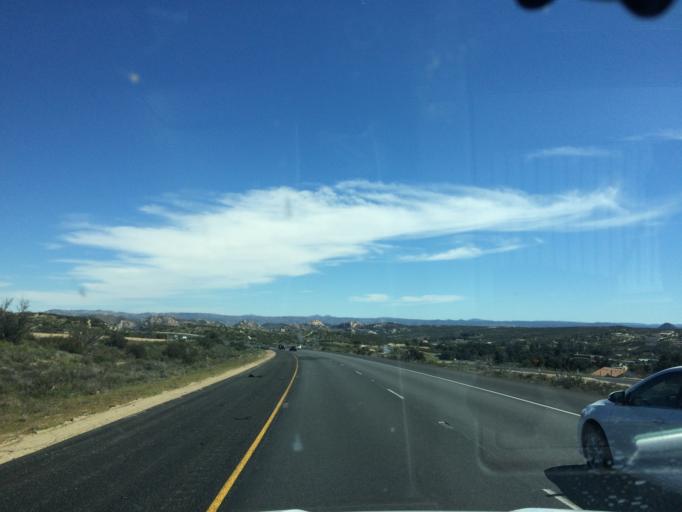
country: US
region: California
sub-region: San Diego County
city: Campo
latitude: 32.6788
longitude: -116.2942
